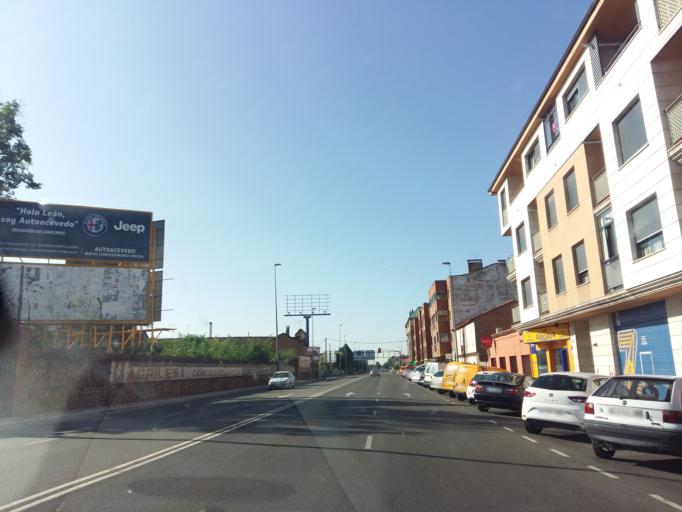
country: ES
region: Castille and Leon
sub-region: Provincia de Leon
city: Leon
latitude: 42.5838
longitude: -5.5842
